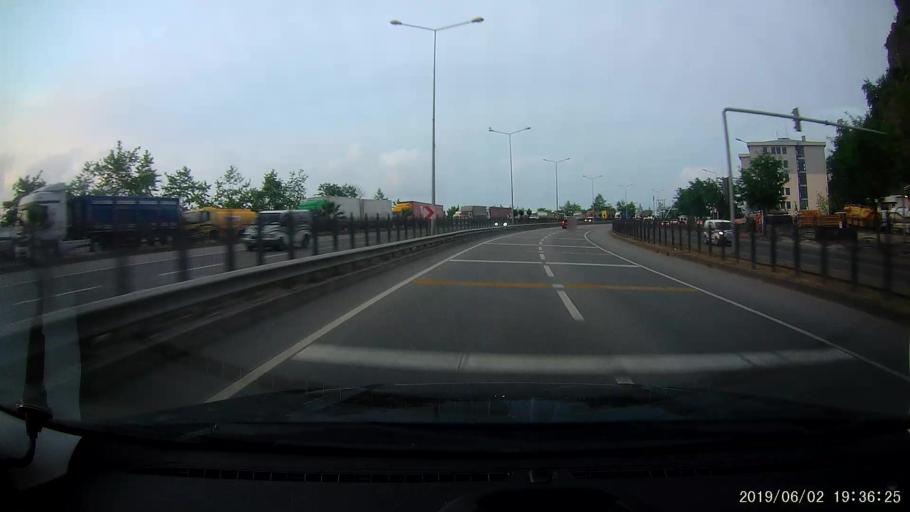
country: TR
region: Giresun
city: Giresun
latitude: 40.9234
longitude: 38.3880
